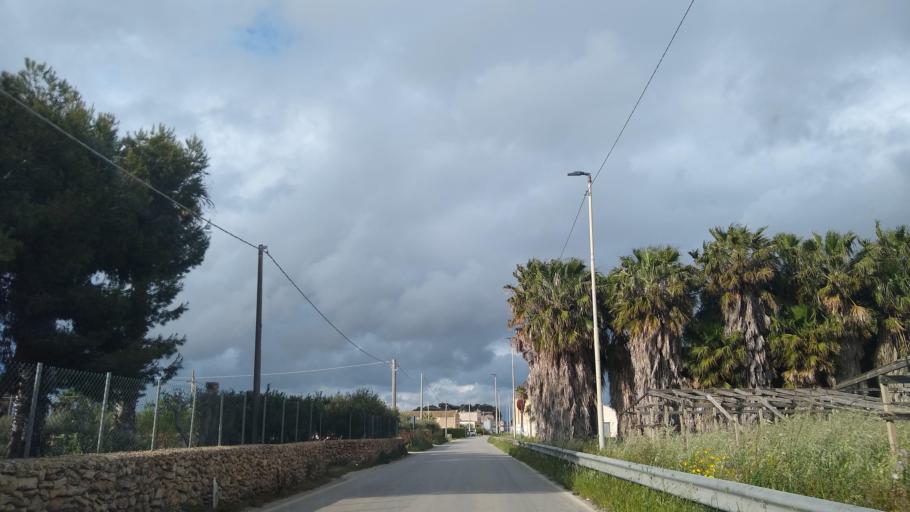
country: IT
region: Sicily
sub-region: Trapani
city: Marsala
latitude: 37.8527
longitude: 12.4852
